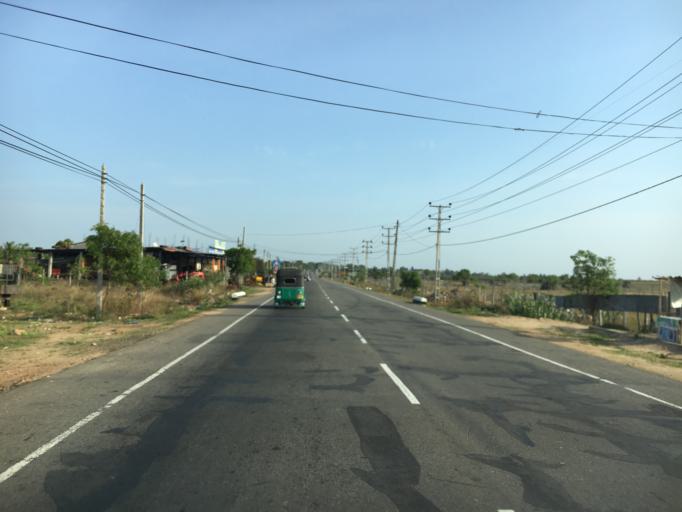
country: LK
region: Eastern Province
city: Eravur Town
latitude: 7.9342
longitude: 81.5106
